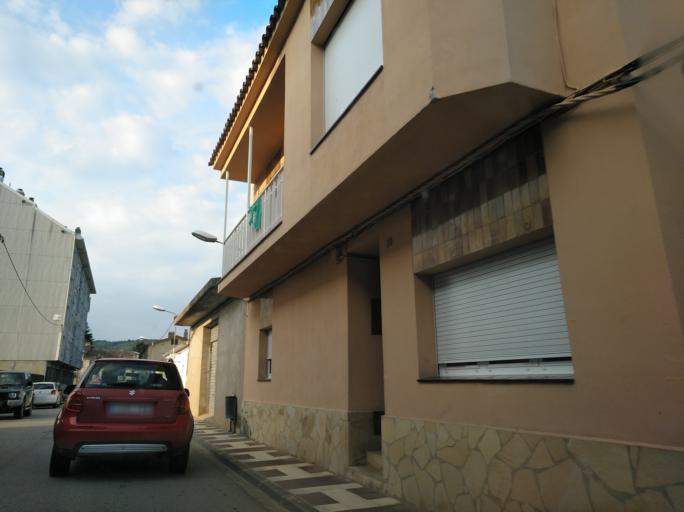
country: ES
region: Catalonia
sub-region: Provincia de Girona
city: la Cellera de Ter
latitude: 41.9678
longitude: 2.6224
